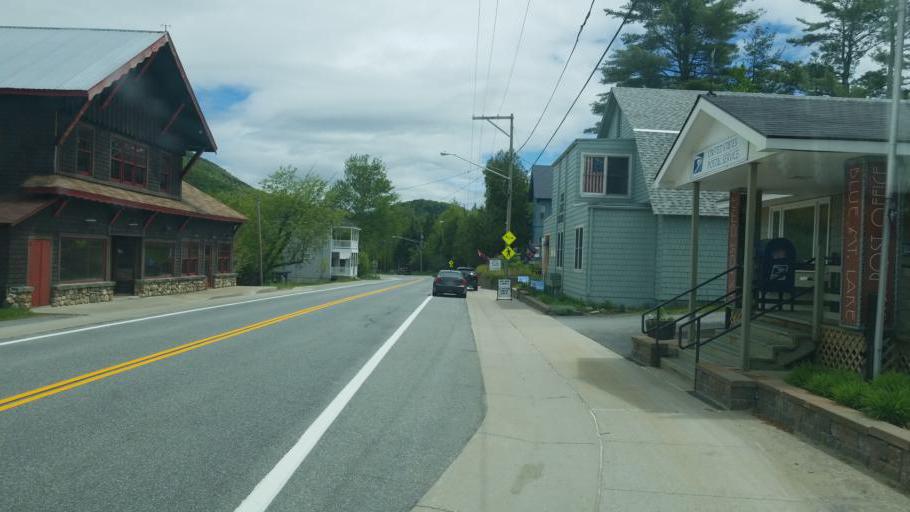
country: US
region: New York
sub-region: Franklin County
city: Tupper Lake
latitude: 43.8543
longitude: -74.4366
